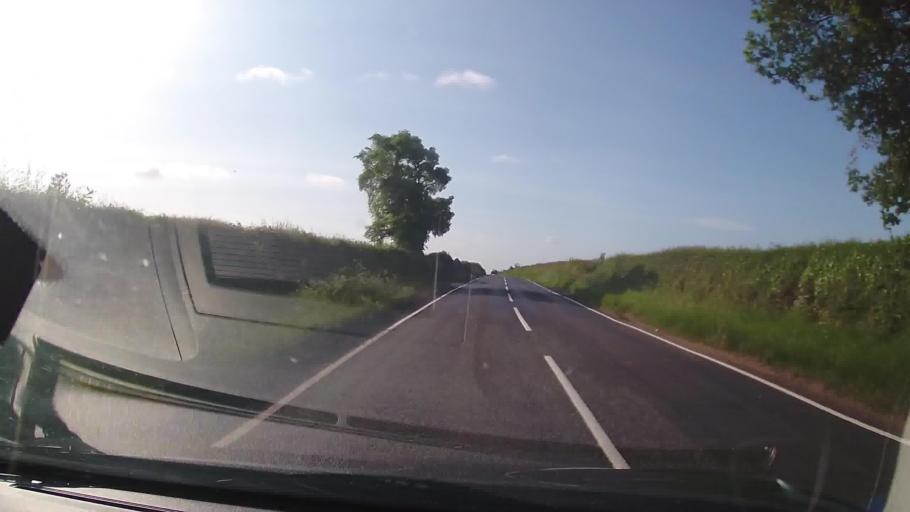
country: GB
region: England
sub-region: Shropshire
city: Wem
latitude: 52.8348
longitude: -2.6998
